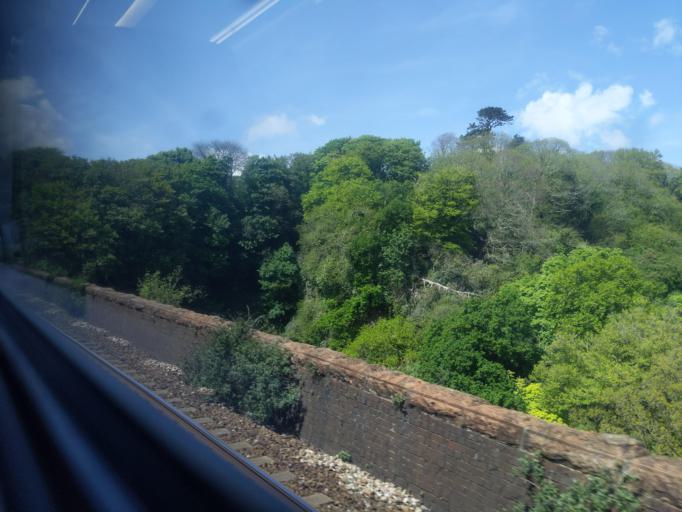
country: GB
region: England
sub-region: Cornwall
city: St Austell
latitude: 50.3426
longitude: -4.7983
